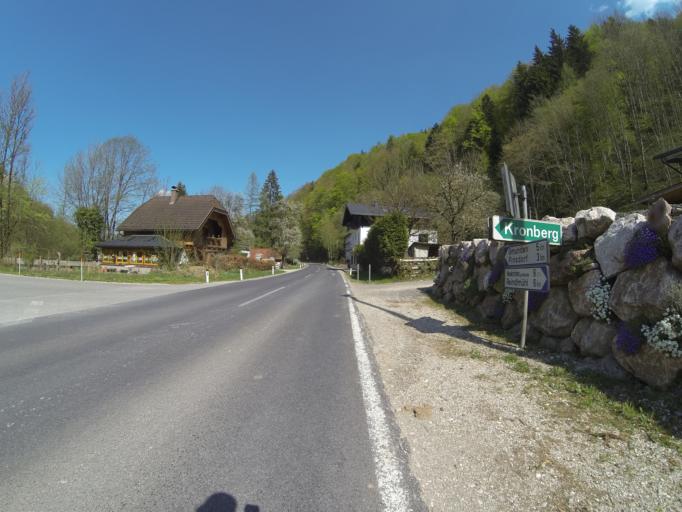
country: AT
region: Upper Austria
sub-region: Politischer Bezirk Gmunden
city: Altmunster
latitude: 47.9238
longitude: 13.7513
